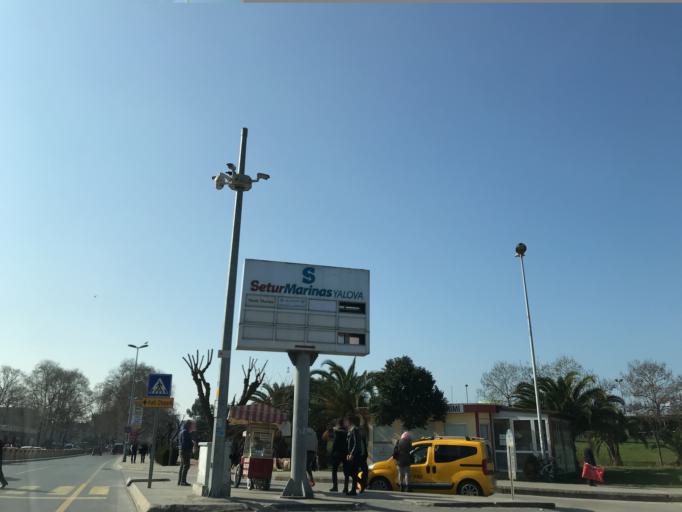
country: TR
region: Yalova
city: Yalova
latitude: 40.6591
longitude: 29.2767
